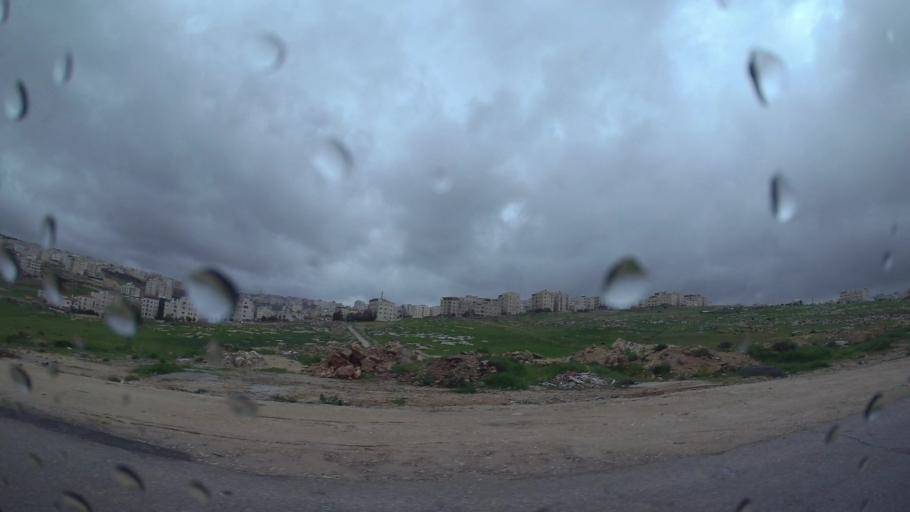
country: JO
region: Amman
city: Al Jubayhah
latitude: 32.0407
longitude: 35.8978
